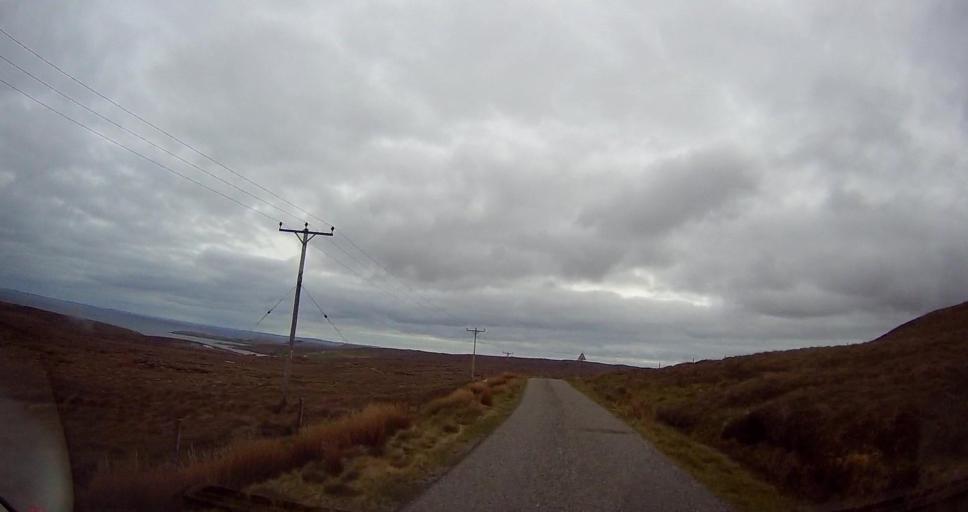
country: GB
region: Scotland
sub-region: Shetland Islands
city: Shetland
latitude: 60.5710
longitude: -1.0669
